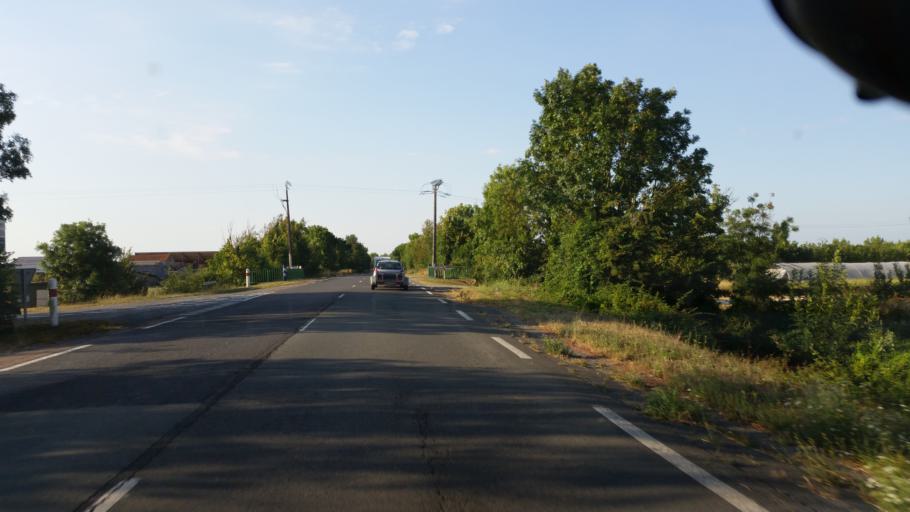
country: FR
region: Poitou-Charentes
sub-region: Departement de la Charente-Maritime
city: Marans
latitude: 46.3328
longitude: -0.9967
